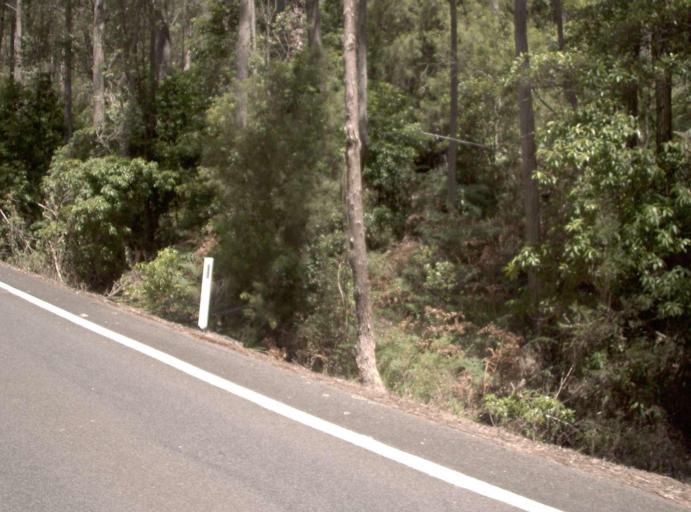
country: AU
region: New South Wales
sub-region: Bombala
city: Bombala
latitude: -37.5824
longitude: 148.9253
